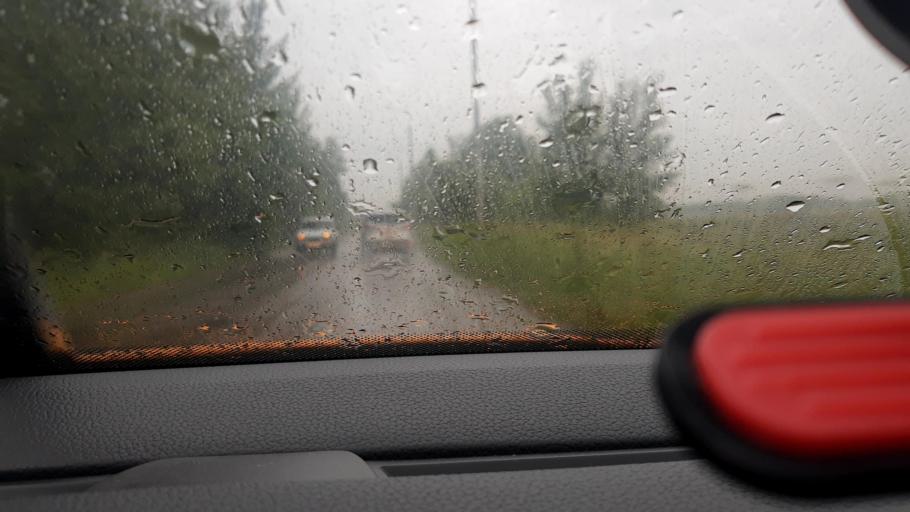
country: RU
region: Moskovskaya
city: Novopodrezkovo
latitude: 55.9362
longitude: 37.3793
